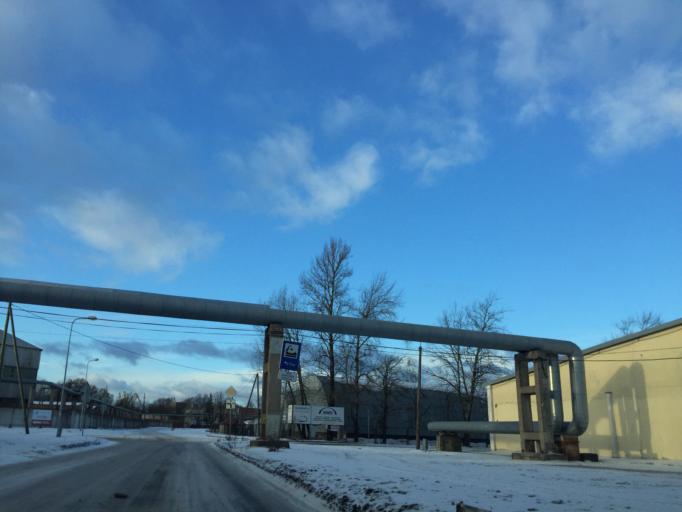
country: LV
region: Riga
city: Riga
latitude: 56.9813
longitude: 24.1114
